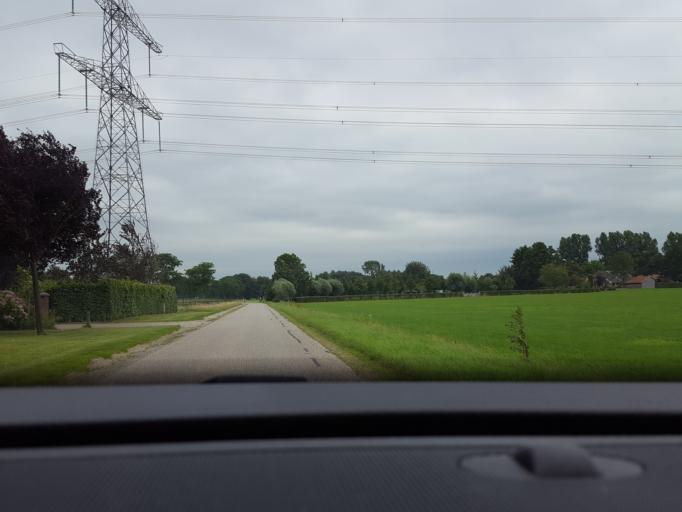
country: NL
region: Gelderland
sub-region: Gemeente Zutphen
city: Leesten
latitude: 52.1200
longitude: 6.2371
